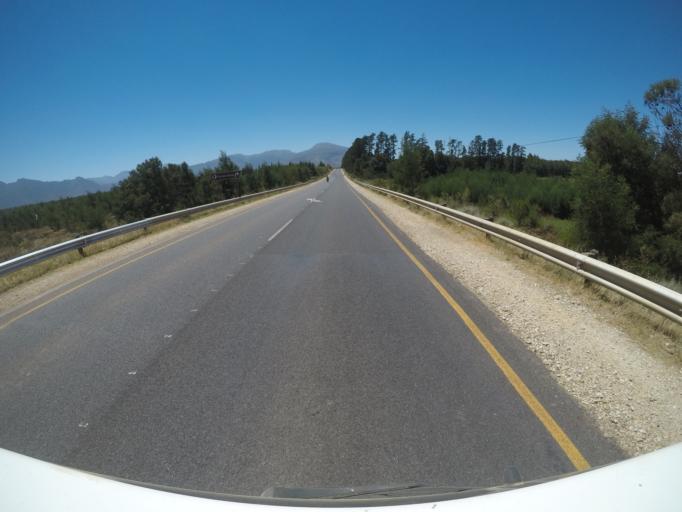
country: ZA
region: Western Cape
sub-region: Overberg District Municipality
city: Grabouw
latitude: -34.0552
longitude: 19.1469
